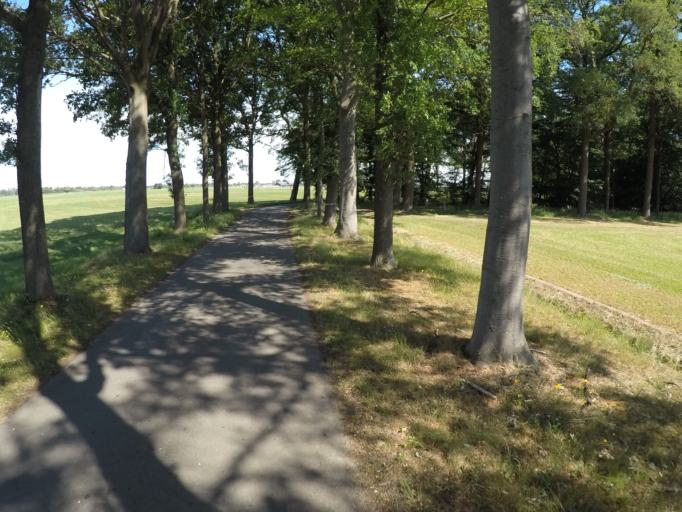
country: BE
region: Flanders
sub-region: Provincie Antwerpen
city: Wuustwezel
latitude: 51.4099
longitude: 4.5498
